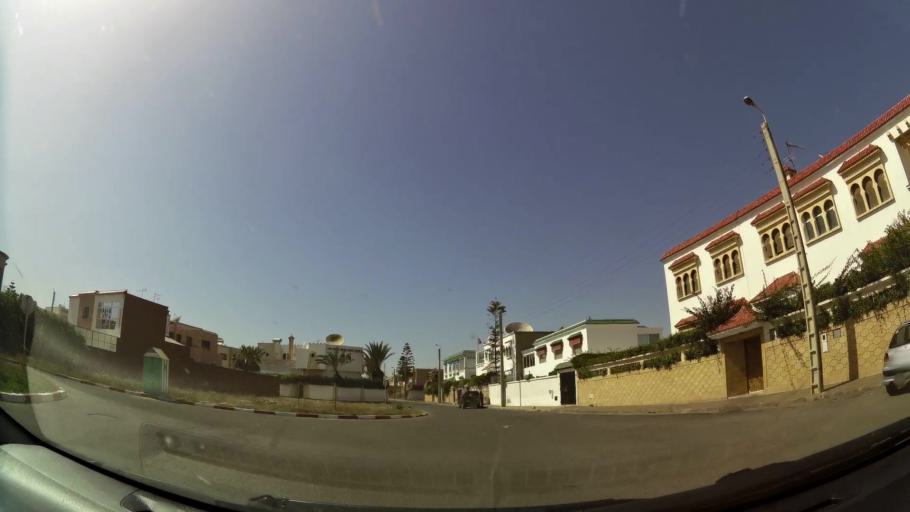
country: MA
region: Souss-Massa-Draa
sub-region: Inezgane-Ait Mellou
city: Inezgane
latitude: 30.3759
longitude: -9.5586
